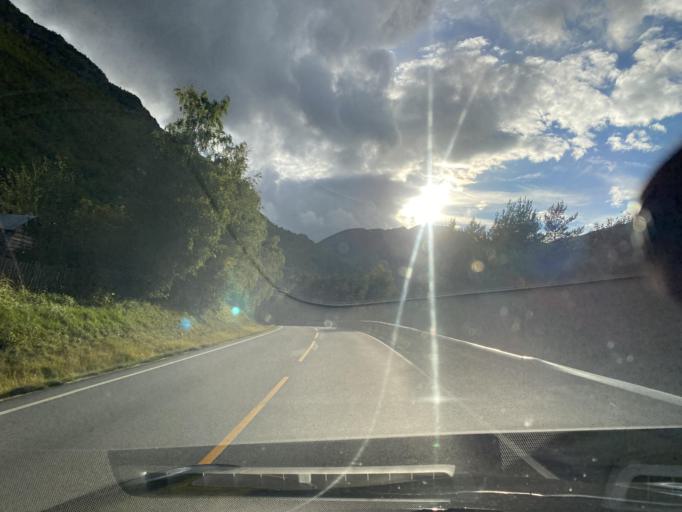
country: NO
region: Oppland
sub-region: Lom
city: Fossbergom
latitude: 61.8113
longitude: 8.4883
